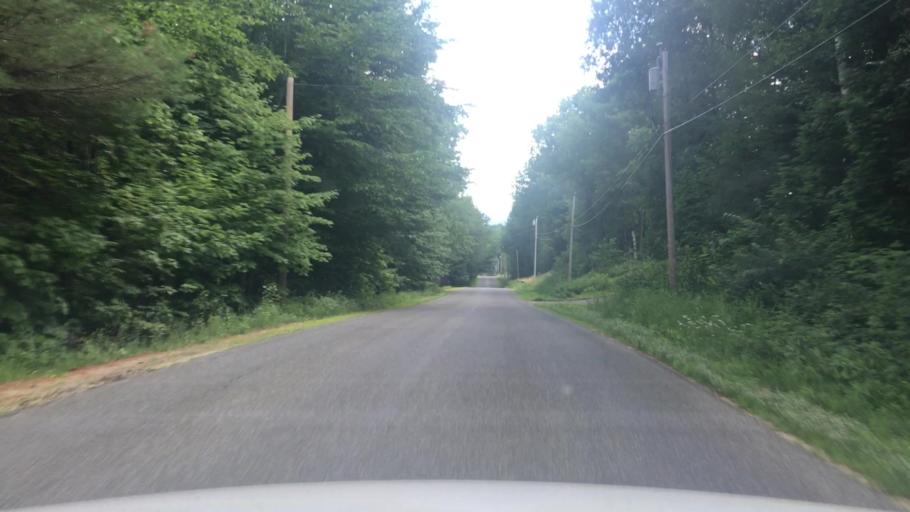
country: US
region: Maine
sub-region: Franklin County
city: Wilton
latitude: 44.6244
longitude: -70.2313
